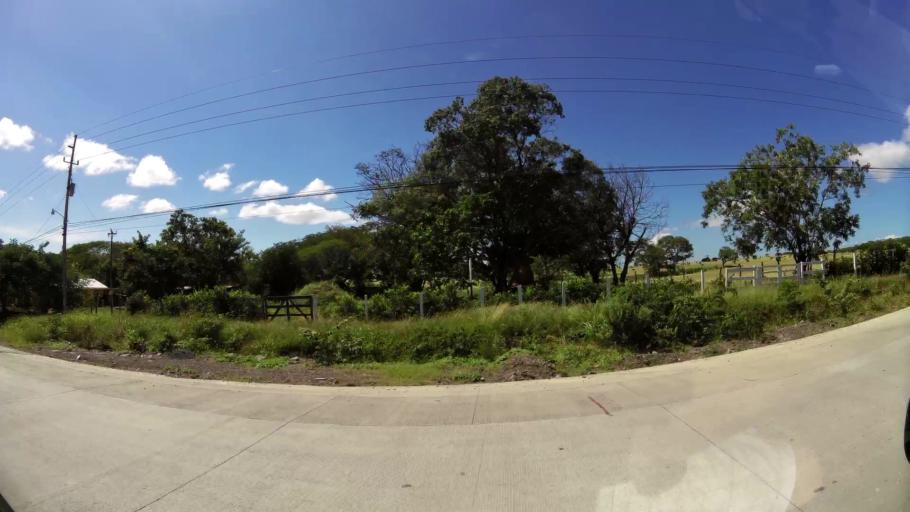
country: CR
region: Guanacaste
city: Bagaces
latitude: 10.5035
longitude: -85.2316
